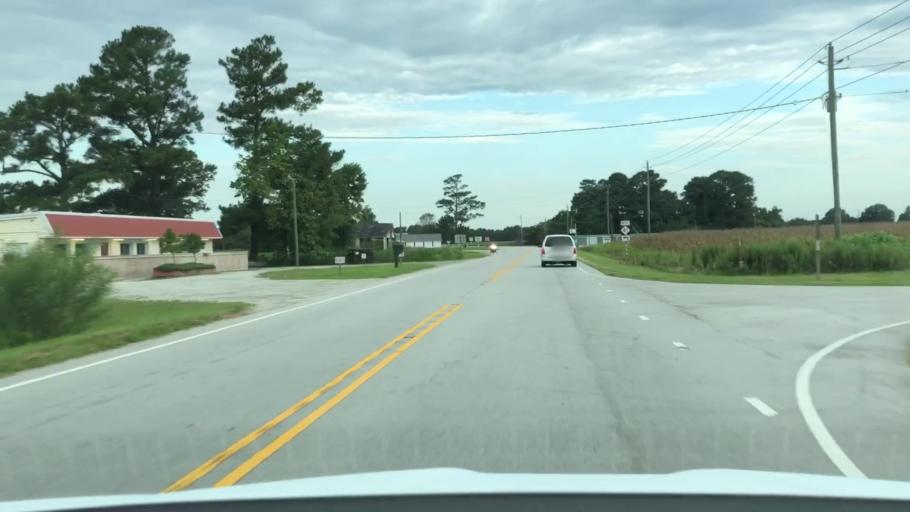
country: US
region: North Carolina
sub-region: Jones County
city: Trenton
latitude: 35.0783
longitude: -77.3991
